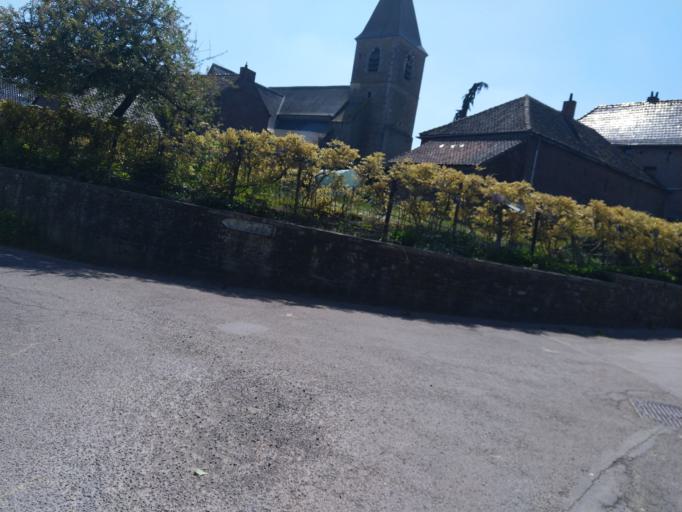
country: BE
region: Wallonia
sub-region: Province du Brabant Wallon
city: Rebecq-Rognon
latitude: 50.6433
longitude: 4.0693
